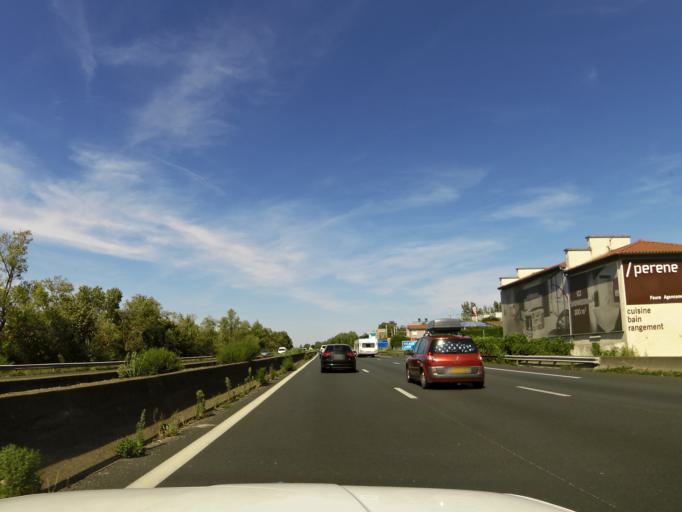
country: FR
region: Rhone-Alpes
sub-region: Departement du Rhone
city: Ternay
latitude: 45.6161
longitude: 4.8105
